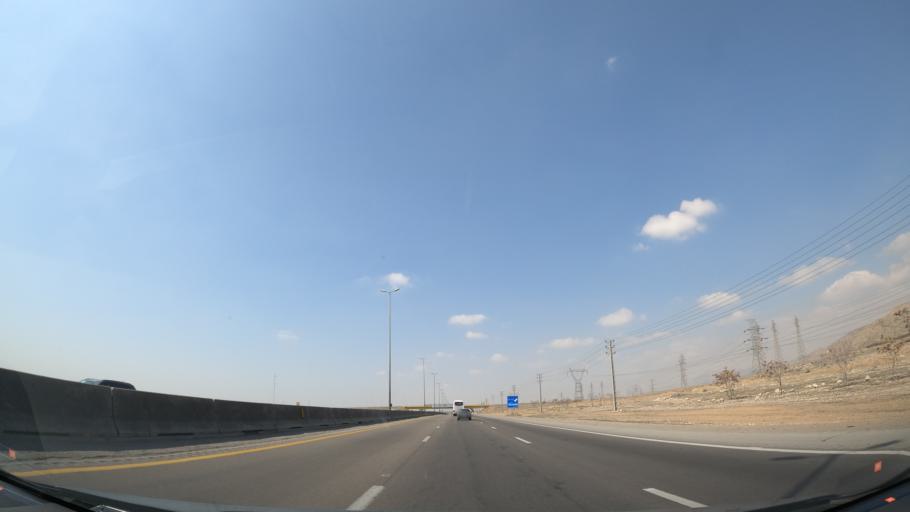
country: IR
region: Qazvin
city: Abyek
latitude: 36.0628
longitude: 50.4935
